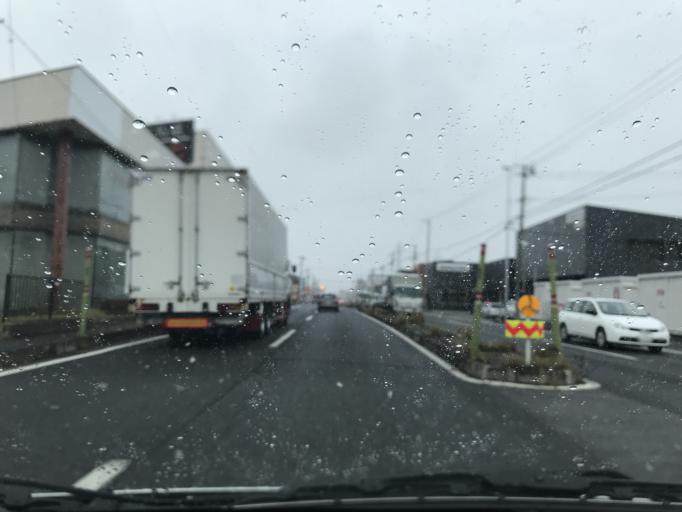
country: JP
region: Iwate
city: Kitakami
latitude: 39.2891
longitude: 141.1042
